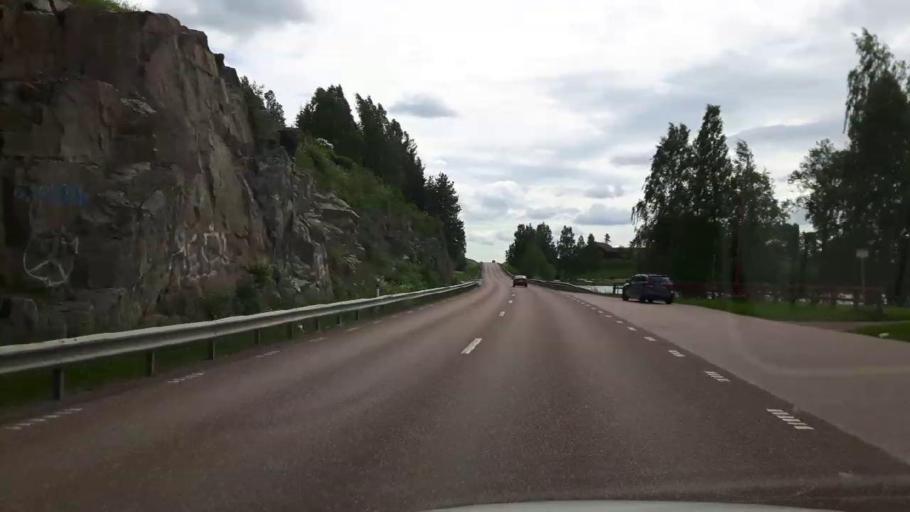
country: SE
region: Dalarna
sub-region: Hedemora Kommun
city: Hedemora
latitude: 60.3235
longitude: 15.9528
